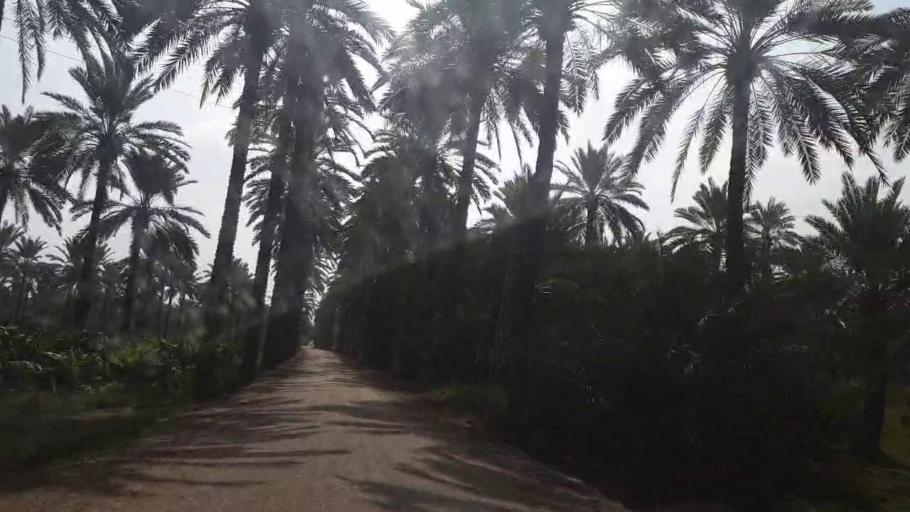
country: PK
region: Sindh
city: Khairpur
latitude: 27.5704
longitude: 68.7513
